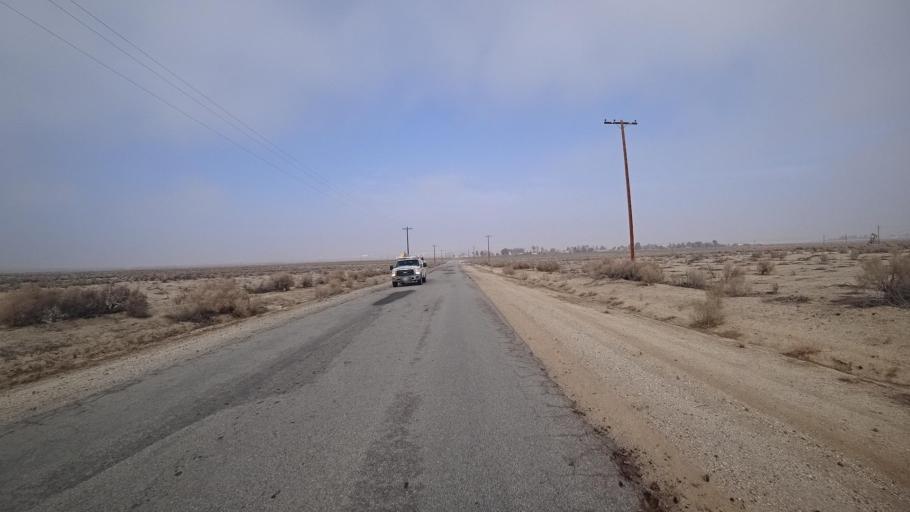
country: US
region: California
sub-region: Kern County
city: Ford City
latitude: 35.2024
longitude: -119.4290
